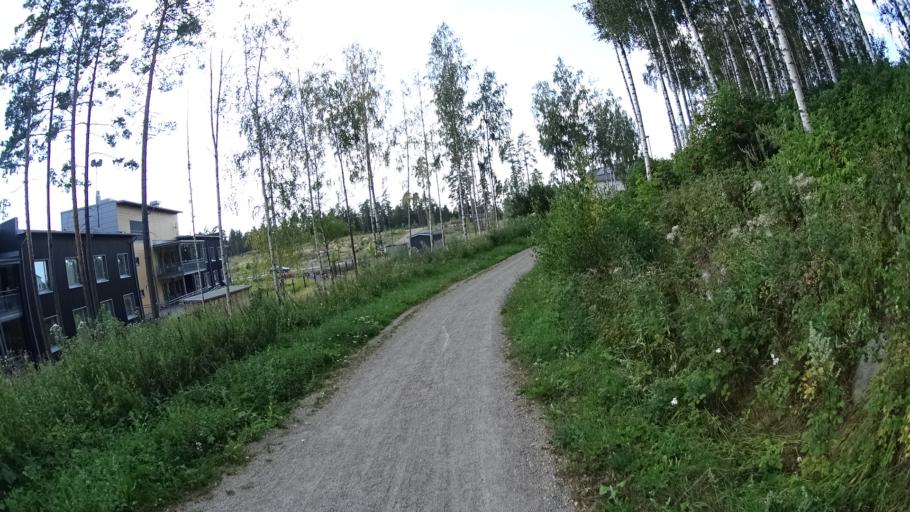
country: FI
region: Uusimaa
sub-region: Porvoo
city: Porvoo
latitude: 60.3786
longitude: 25.7050
